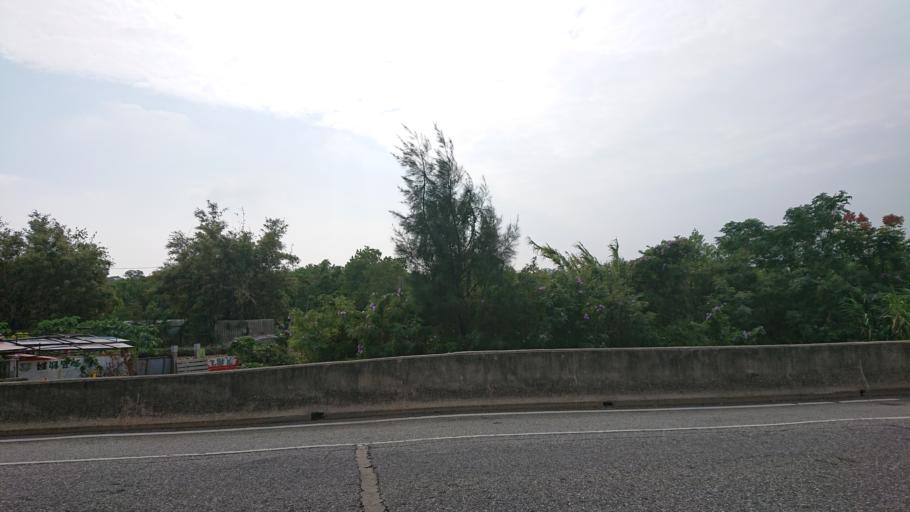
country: TW
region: Fukien
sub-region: Kinmen
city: Jincheng
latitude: 24.4491
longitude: 118.3837
